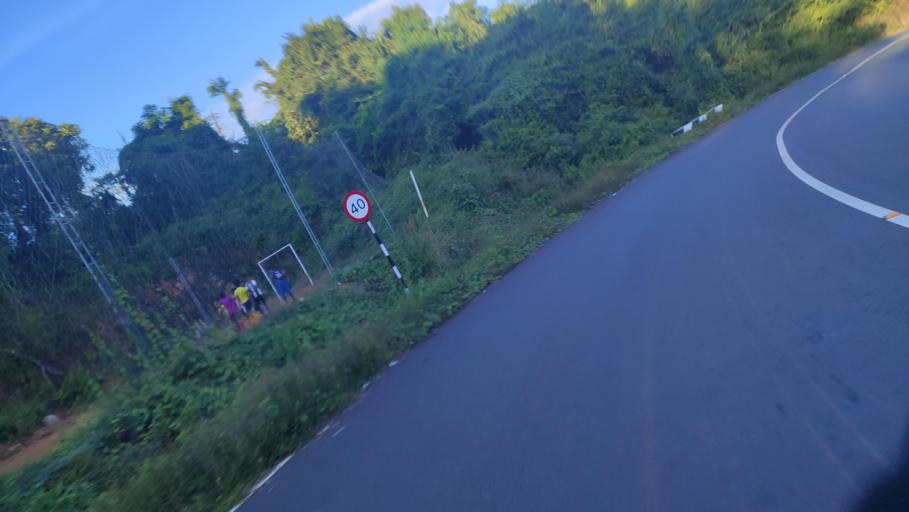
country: IN
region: Kerala
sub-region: Kasaragod District
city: Kasaragod
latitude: 12.4628
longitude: 75.0867
